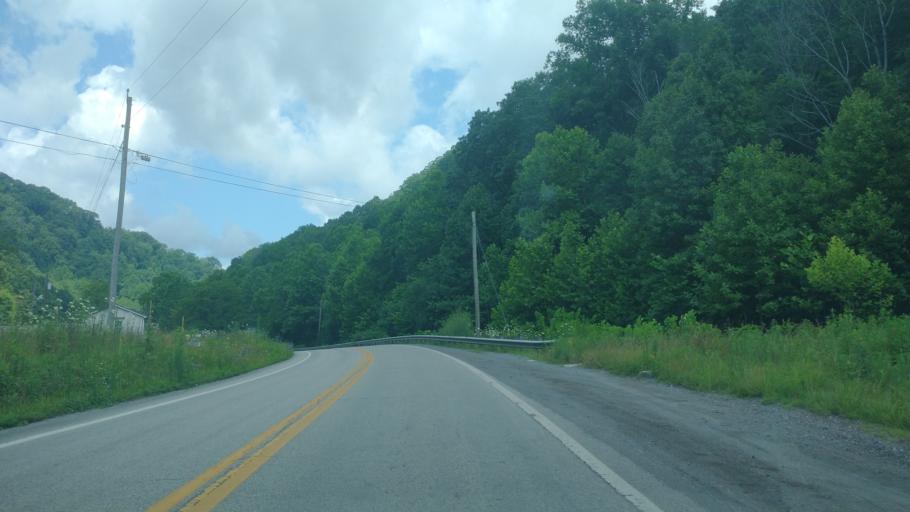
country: US
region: West Virginia
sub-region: McDowell County
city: Welch
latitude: 37.4132
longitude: -81.4774
